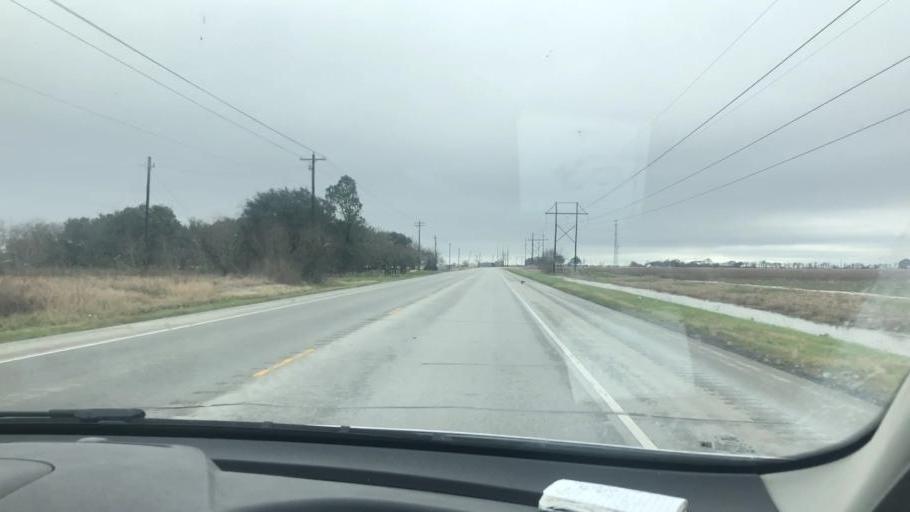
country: US
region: Texas
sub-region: Wharton County
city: Boling
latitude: 29.1485
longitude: -95.9888
